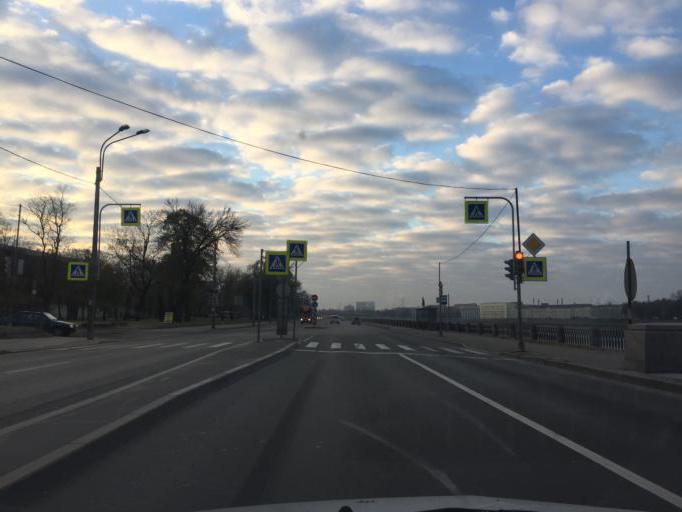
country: RU
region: St.-Petersburg
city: Obukhovo
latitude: 59.8889
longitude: 30.4483
